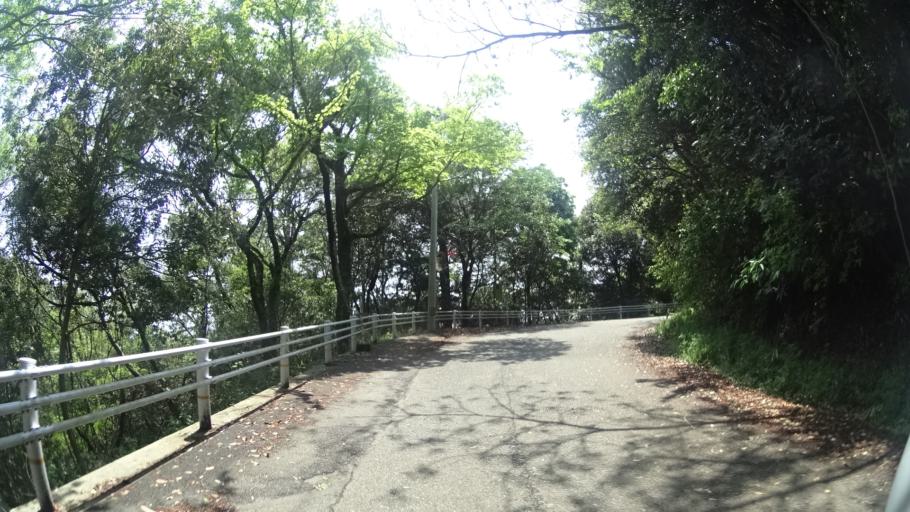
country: JP
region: Tokushima
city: Tokushima-shi
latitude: 34.0663
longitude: 134.5286
